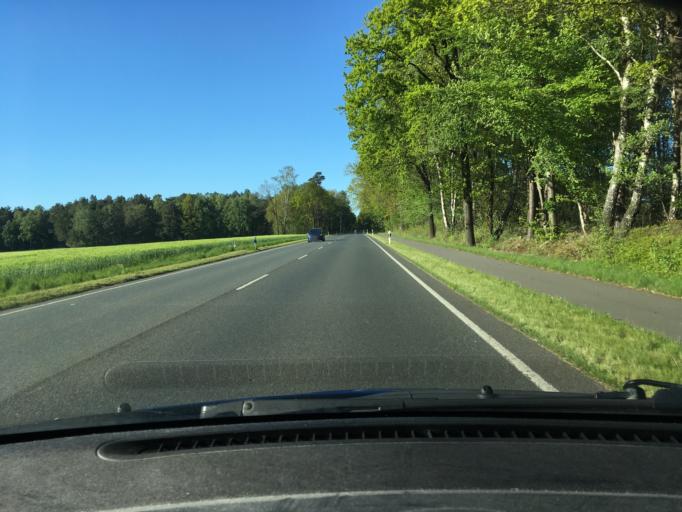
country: DE
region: Lower Saxony
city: Soltau
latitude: 53.0420
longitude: 9.8556
